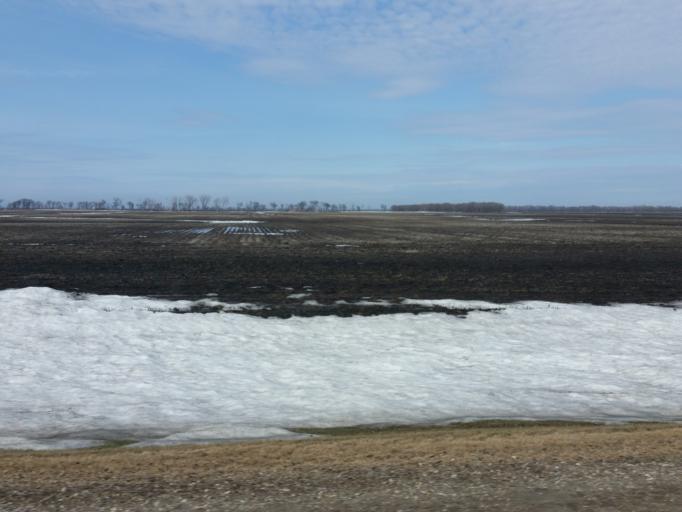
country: US
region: North Dakota
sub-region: Walsh County
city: Grafton
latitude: 48.4265
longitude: -97.2269
